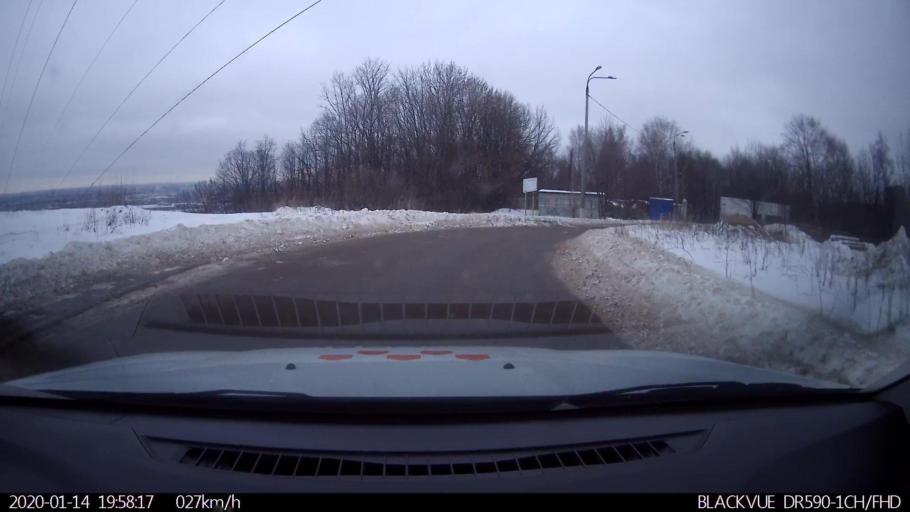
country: RU
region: Nizjnij Novgorod
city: Nizhniy Novgorod
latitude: 56.2367
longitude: 43.9395
